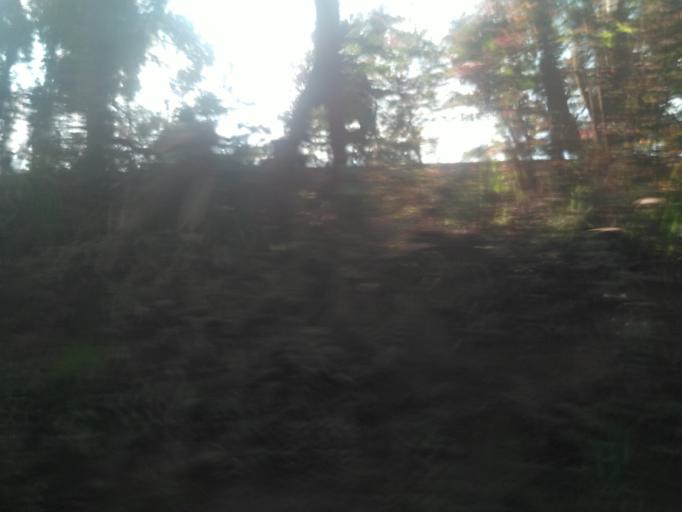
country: UG
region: Central Region
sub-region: Wakiso District
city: Kajansi
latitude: 0.2886
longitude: 32.4550
